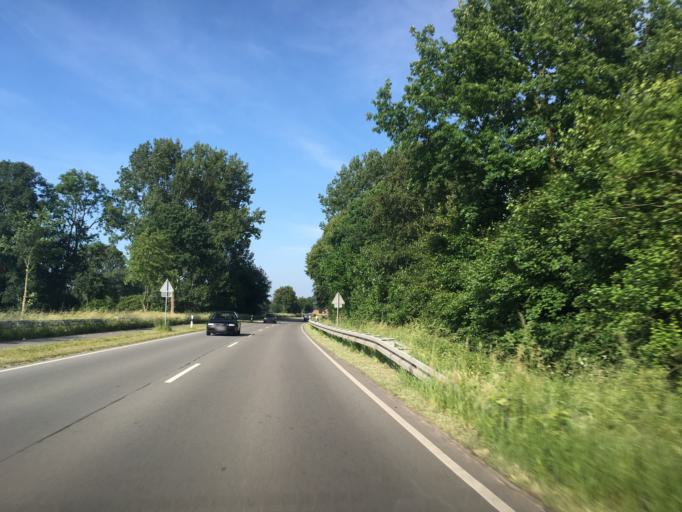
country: DE
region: North Rhine-Westphalia
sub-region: Regierungsbezirk Munster
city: Greven
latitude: 52.0923
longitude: 7.5480
